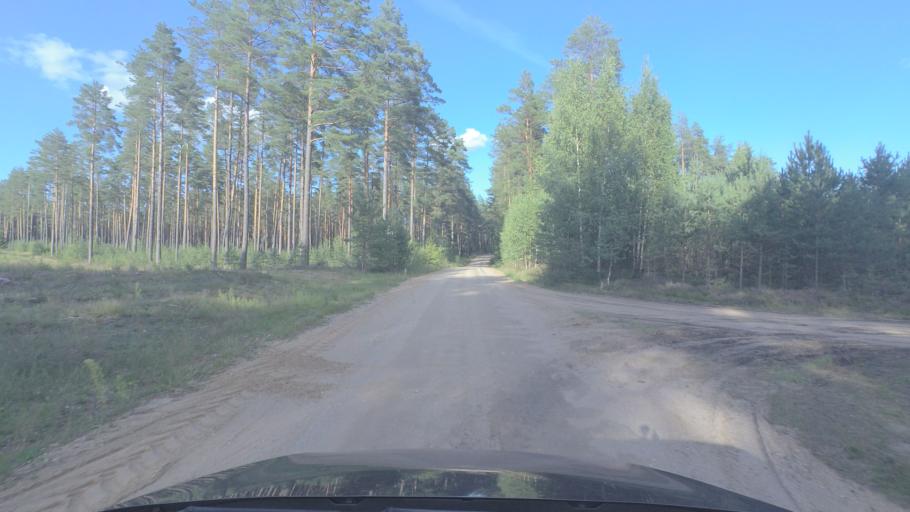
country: LT
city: Pabrade
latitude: 55.1610
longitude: 25.8136
